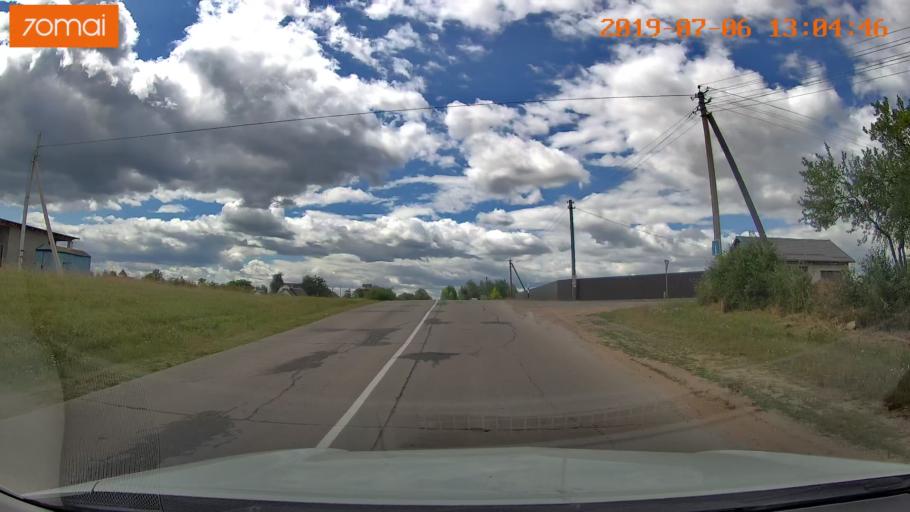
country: BY
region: Minsk
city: Dzyarzhynsk
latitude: 53.6897
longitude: 27.0771
